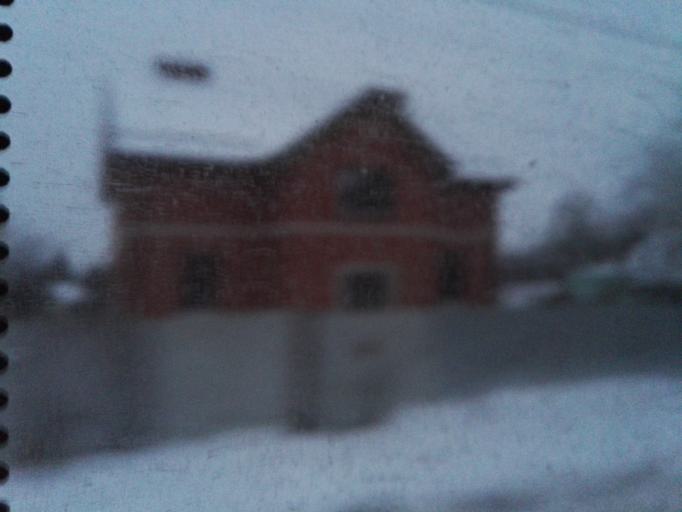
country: RU
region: Tula
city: Tula
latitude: 54.1662
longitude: 37.6067
